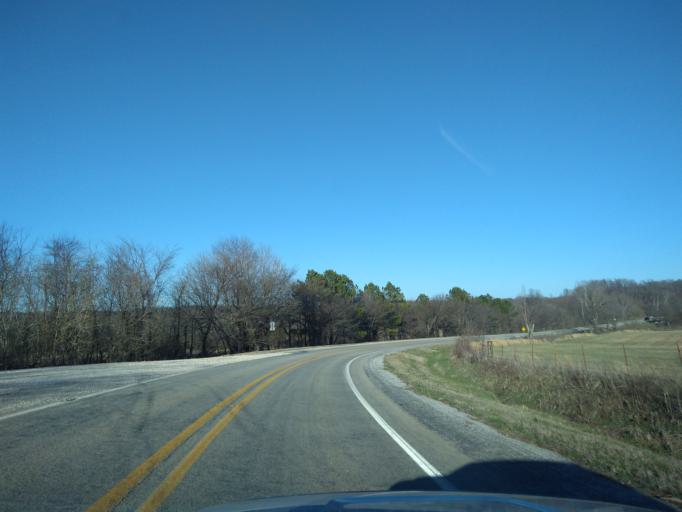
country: US
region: Arkansas
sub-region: Washington County
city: Farmington
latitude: 36.1027
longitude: -94.3486
